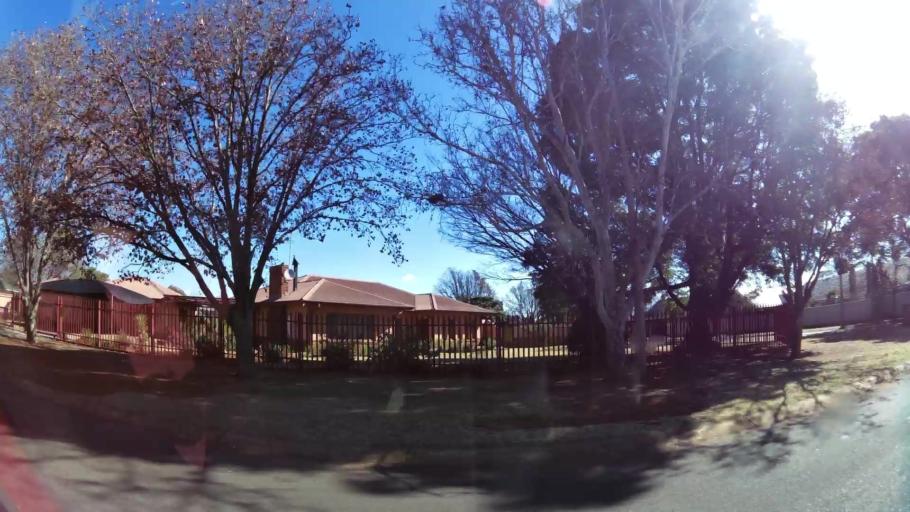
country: ZA
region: Gauteng
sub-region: West Rand District Municipality
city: Carletonville
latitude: -26.3506
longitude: 27.3875
